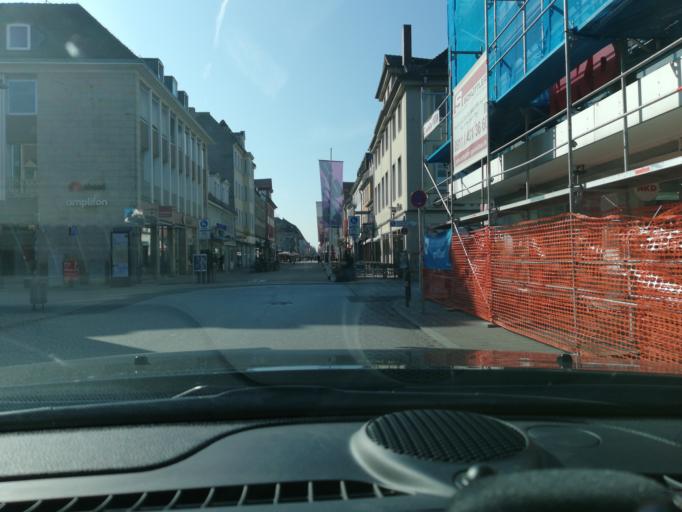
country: DE
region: Bavaria
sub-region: Regierungsbezirk Mittelfranken
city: Erlangen
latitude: 49.5992
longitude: 11.0032
